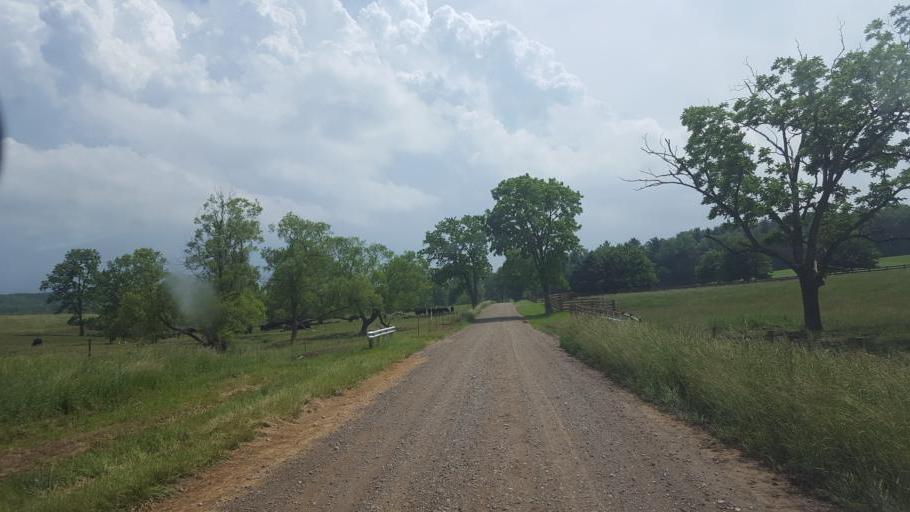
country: US
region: Ohio
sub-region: Knox County
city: Oak Hill
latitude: 40.3148
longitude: -82.2401
